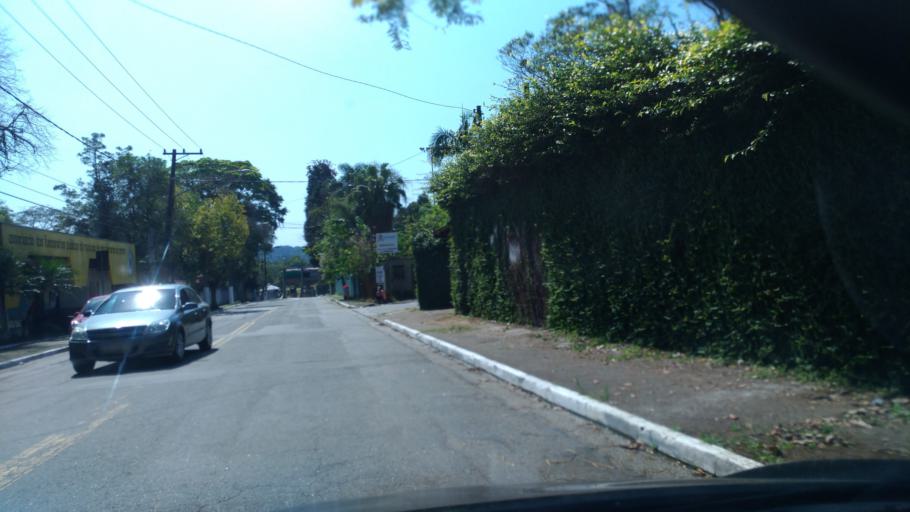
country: BR
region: Sao Paulo
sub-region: Sao Bernardo Do Campo
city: Sao Bernardo do Campo
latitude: -23.7717
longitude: -46.5214
